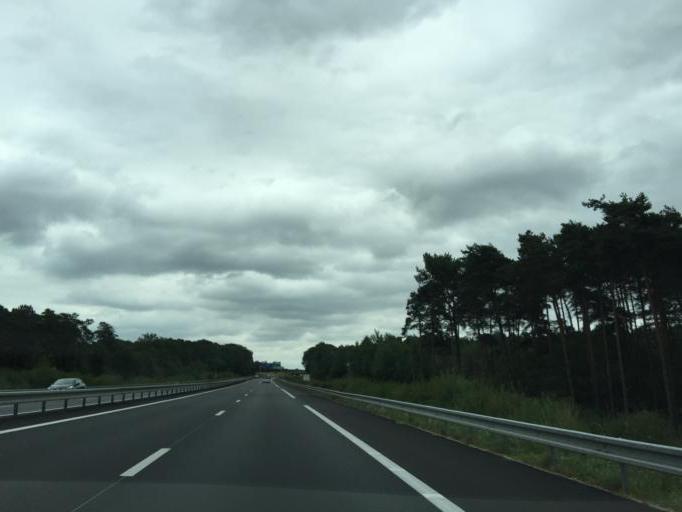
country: FR
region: Pays de la Loire
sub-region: Departement de la Sarthe
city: Champagne
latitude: 48.0055
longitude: 0.3062
